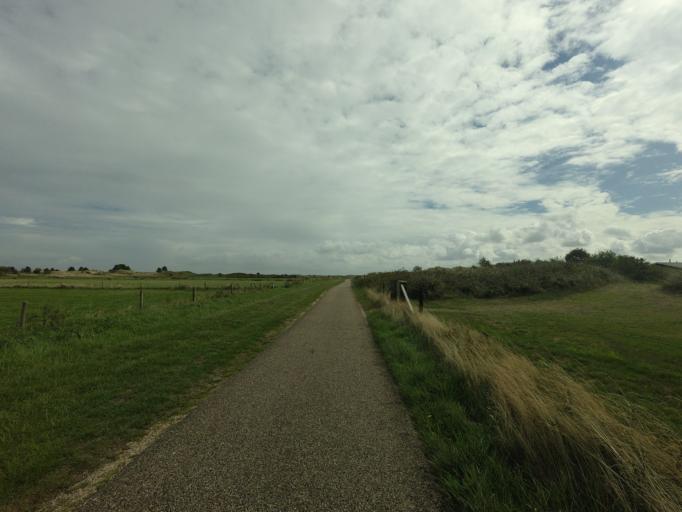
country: NL
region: Friesland
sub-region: Gemeente Ameland
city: Nes
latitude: 53.4554
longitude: 5.8172
